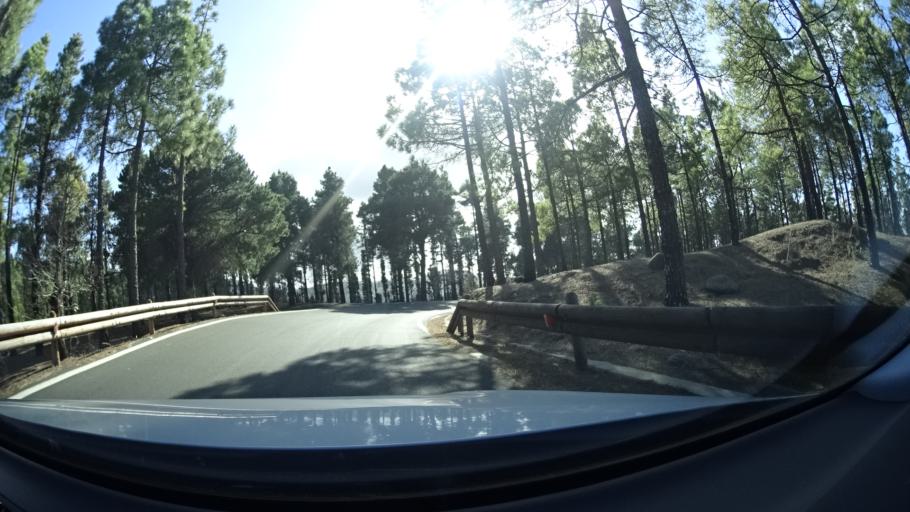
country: ES
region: Canary Islands
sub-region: Provincia de Las Palmas
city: Tejeda
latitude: 27.9740
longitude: -15.5777
